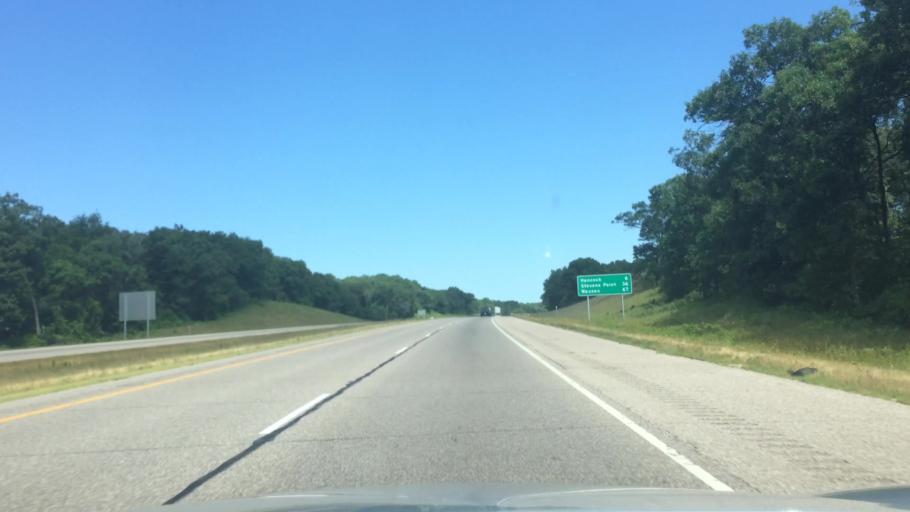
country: US
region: Wisconsin
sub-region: Marquette County
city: Westfield
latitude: 44.0457
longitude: -89.5379
